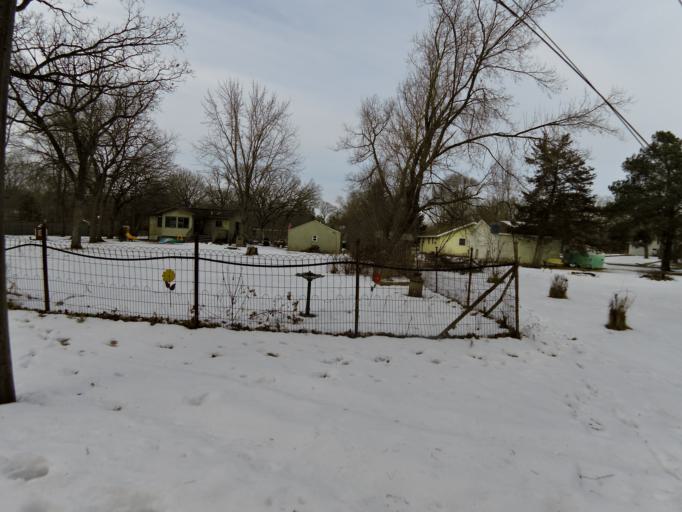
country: US
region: Minnesota
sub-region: Washington County
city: Lake Saint Croix Beach
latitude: 44.9159
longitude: -92.7722
